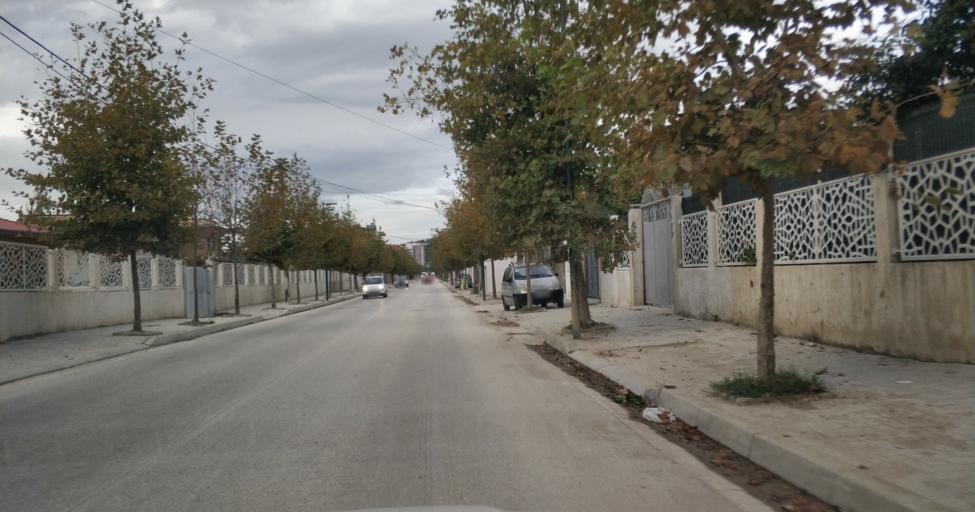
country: AL
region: Vlore
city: Vlore
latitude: 40.4507
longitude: 19.4971
